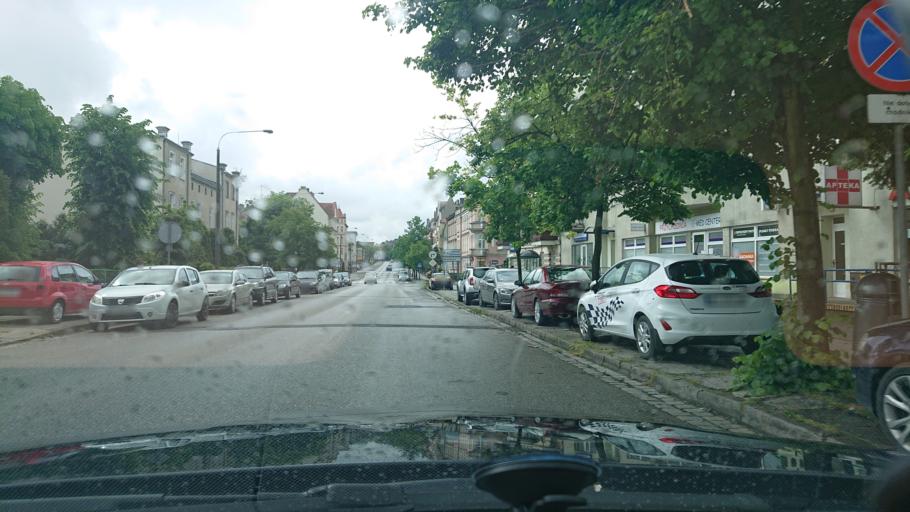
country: PL
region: Greater Poland Voivodeship
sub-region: Powiat gnieznienski
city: Gniezno
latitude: 52.5402
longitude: 17.6004
